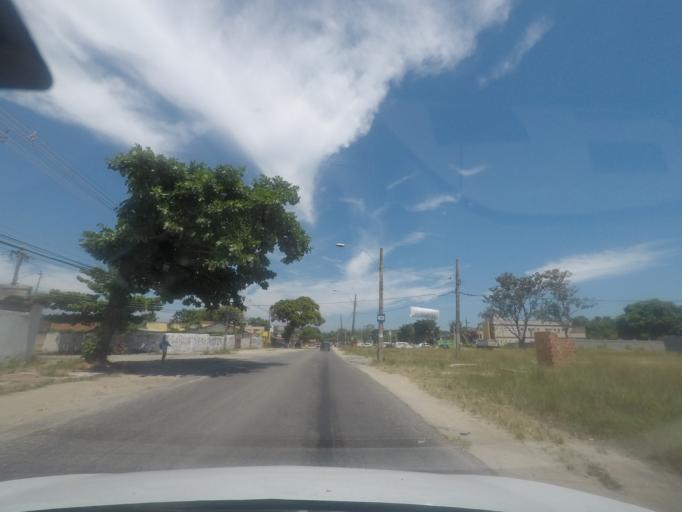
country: BR
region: Rio de Janeiro
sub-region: Itaguai
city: Itaguai
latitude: -22.9827
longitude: -43.6623
